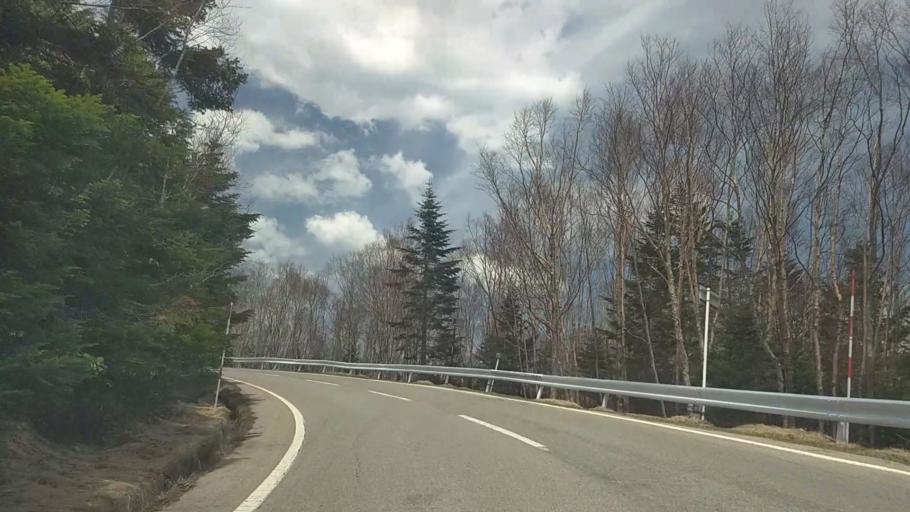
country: JP
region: Nagano
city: Saku
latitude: 36.0573
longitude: 138.3545
